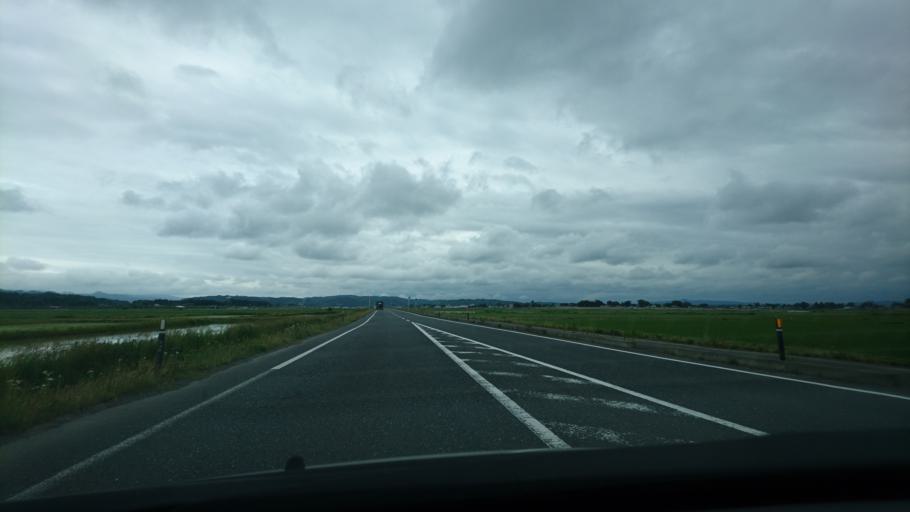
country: JP
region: Miyagi
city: Wakuya
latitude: 38.6890
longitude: 141.2608
